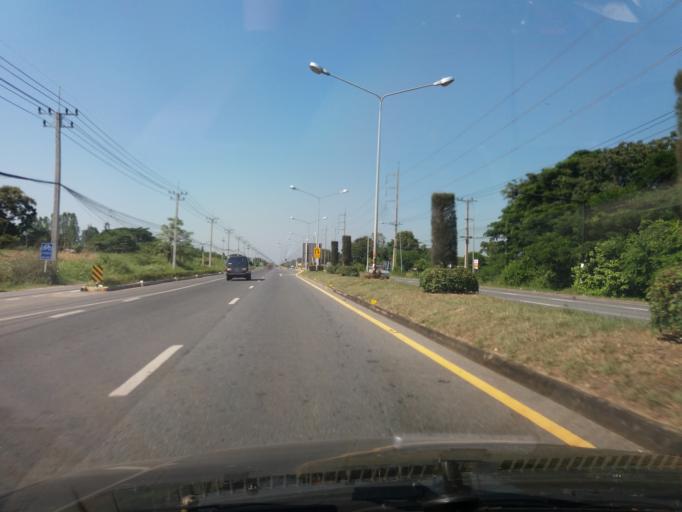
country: TH
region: Chai Nat
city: Chai Nat
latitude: 15.2089
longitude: 100.1194
